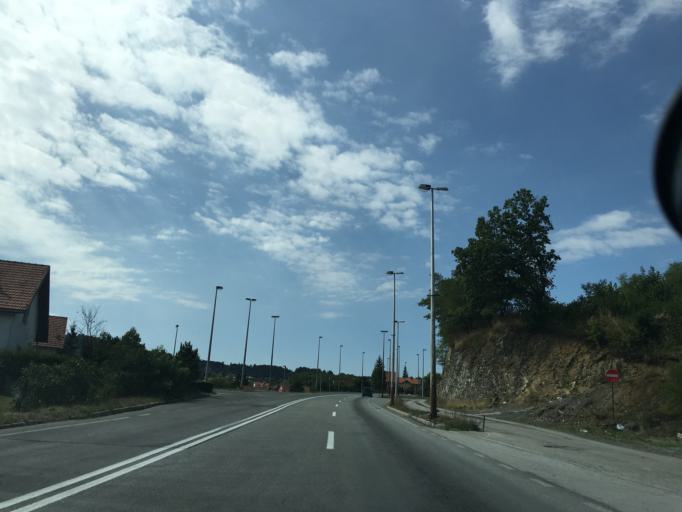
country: RS
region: Central Serbia
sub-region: Zlatiborski Okrug
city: Cajetina
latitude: 43.7544
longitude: 19.7156
